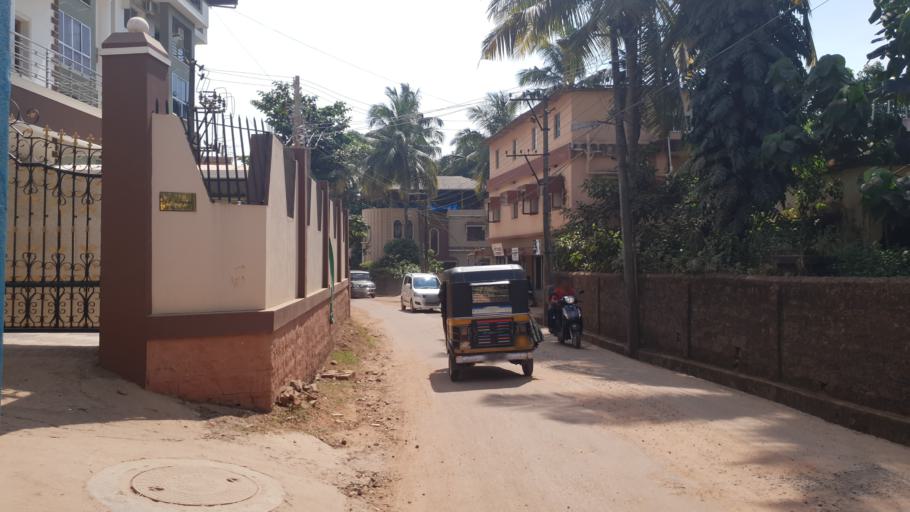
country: IN
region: Karnataka
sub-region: Dakshina Kannada
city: Ullal
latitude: 12.8465
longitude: 74.8466
